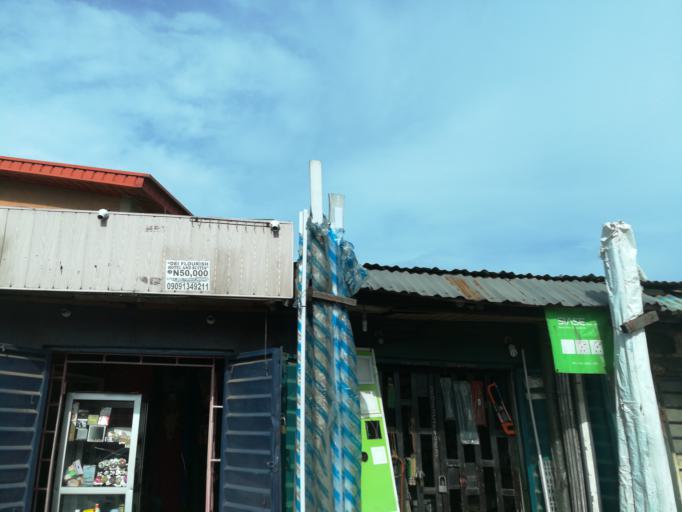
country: NG
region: Lagos
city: Oshodi
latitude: 6.5566
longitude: 3.3453
